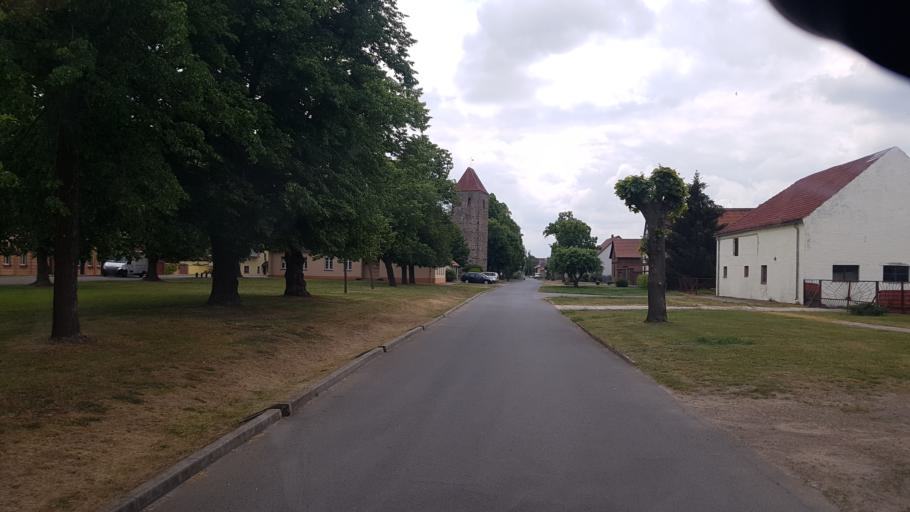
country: DE
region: Brandenburg
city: Ihlow
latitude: 51.8863
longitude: 13.3771
